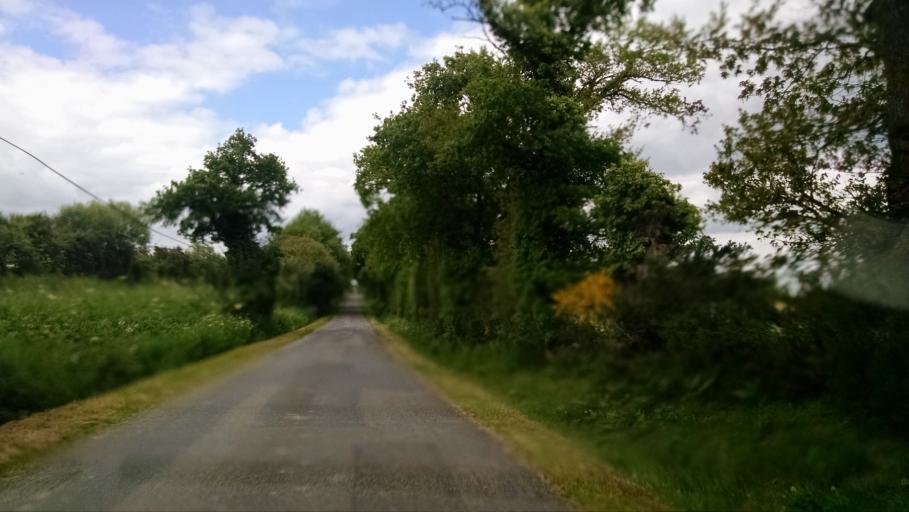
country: FR
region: Pays de la Loire
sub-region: Departement de la Loire-Atlantique
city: Remouille
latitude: 47.0393
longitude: -1.3833
